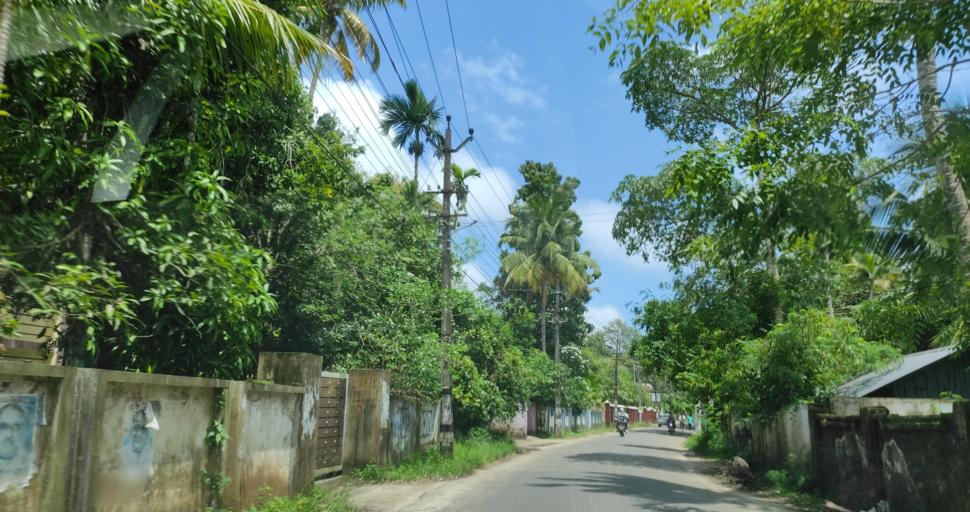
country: IN
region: Kerala
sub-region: Alappuzha
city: Vayalar
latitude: 9.7043
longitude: 76.3390
